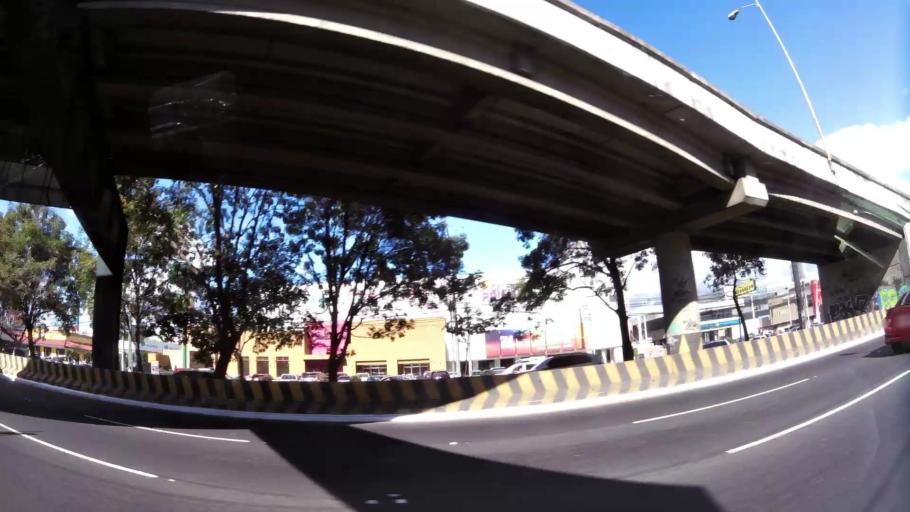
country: GT
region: Guatemala
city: Guatemala City
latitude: 14.6232
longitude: -90.5522
